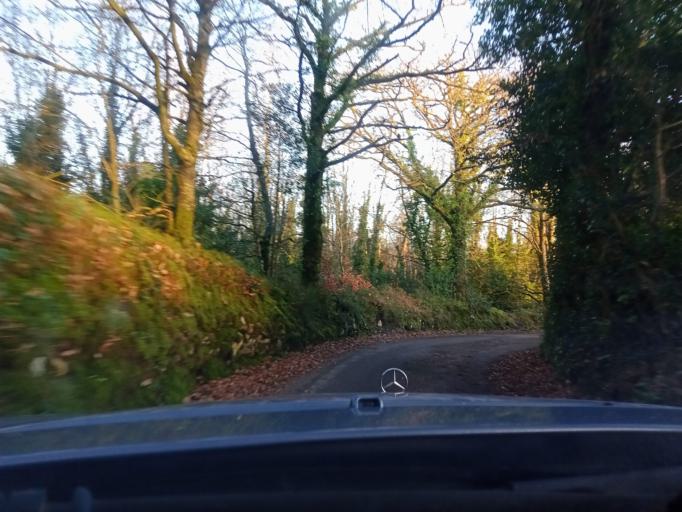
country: IE
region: Leinster
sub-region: Kilkenny
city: Graiguenamanagh
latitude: 52.4832
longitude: -6.9505
